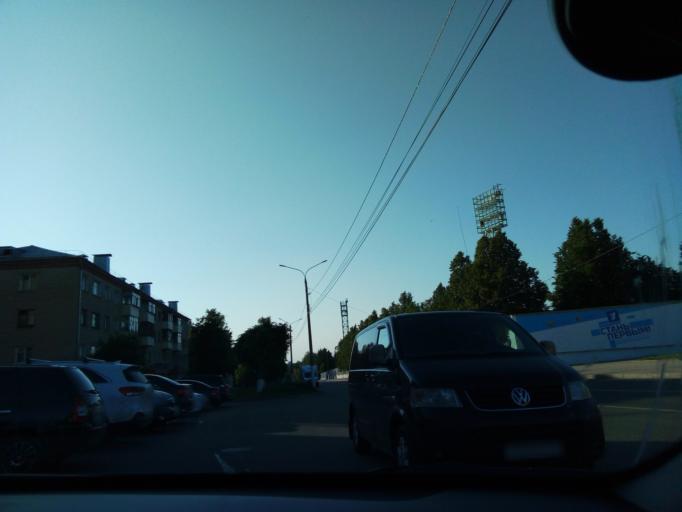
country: RU
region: Chuvashia
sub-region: Cheboksarskiy Rayon
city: Cheboksary
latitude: 56.1219
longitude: 47.2642
